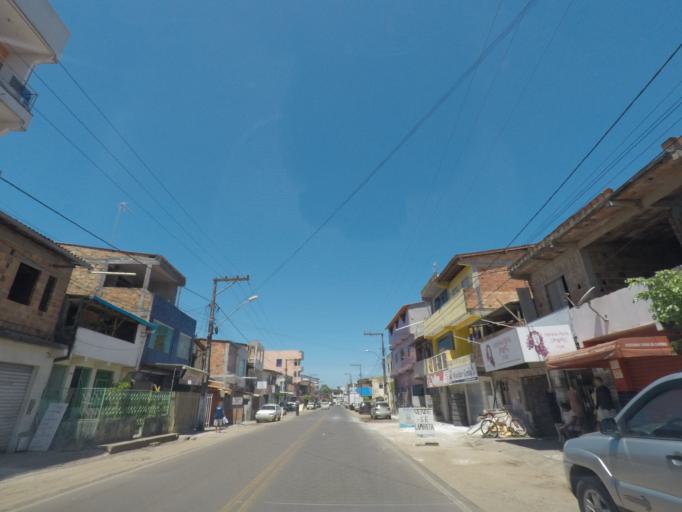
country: BR
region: Bahia
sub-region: Valenca
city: Valenca
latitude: -13.3569
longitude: -39.0637
